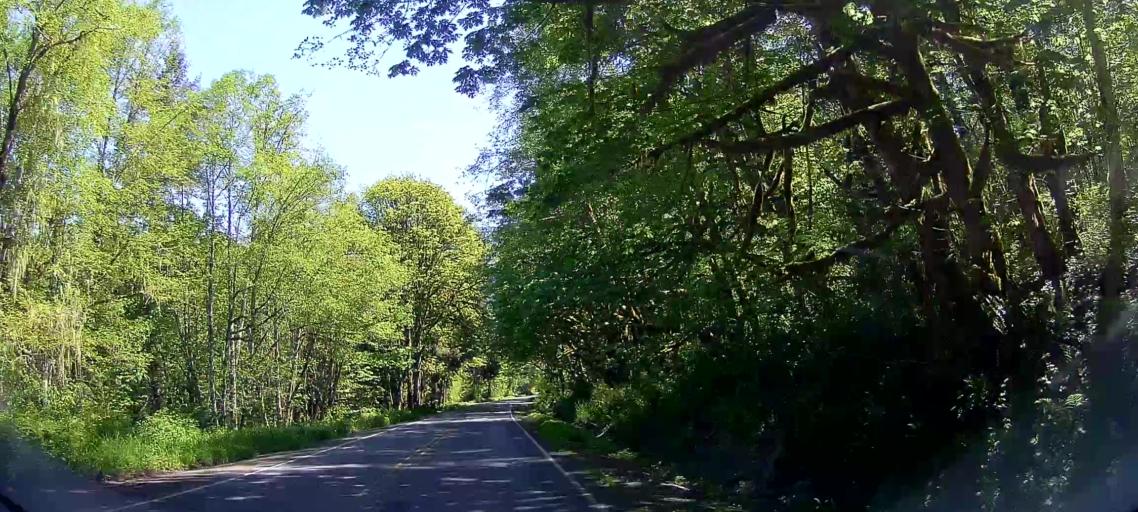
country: US
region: Washington
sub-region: Snohomish County
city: Darrington
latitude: 48.5087
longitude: -121.6864
